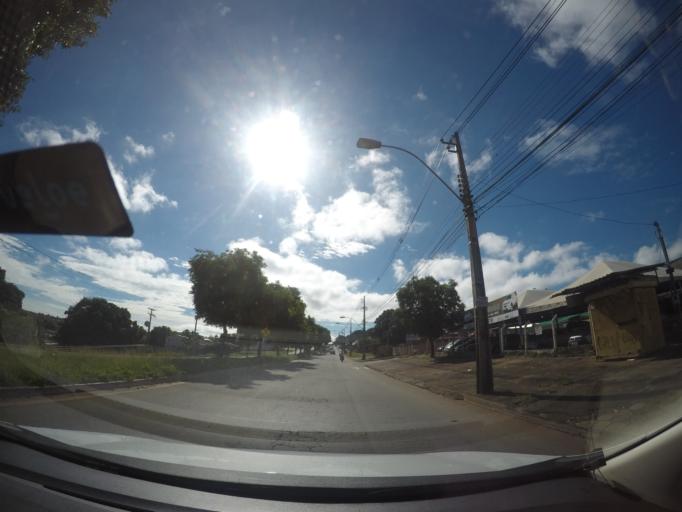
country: BR
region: Goias
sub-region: Goiania
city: Goiania
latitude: -16.6591
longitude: -49.1916
